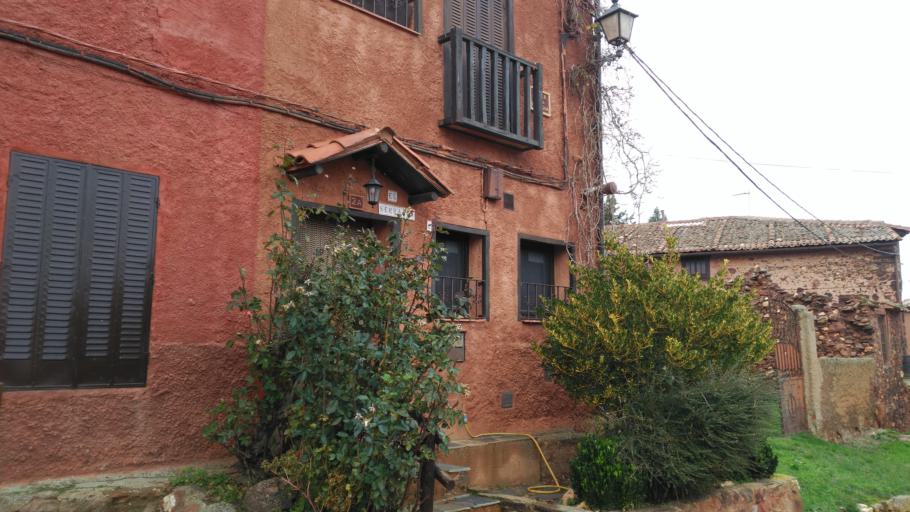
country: ES
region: Castille and Leon
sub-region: Provincia de Soria
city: Liceras
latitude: 41.3146
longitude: -3.3314
